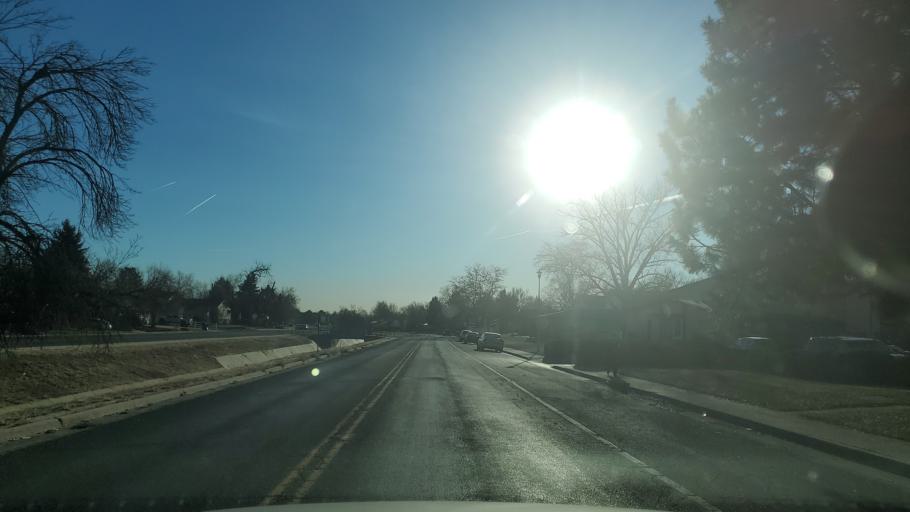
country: US
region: Colorado
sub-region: Adams County
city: Welby
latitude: 39.8458
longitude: -104.9747
